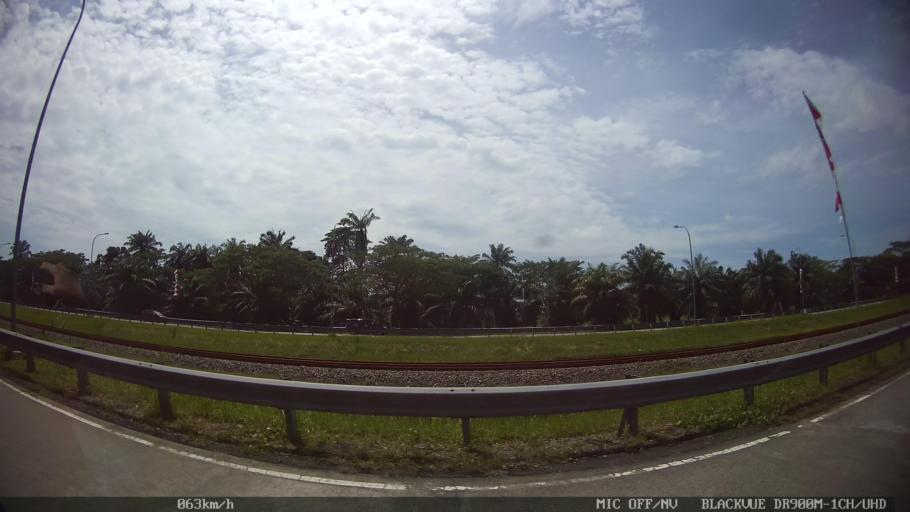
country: ID
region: North Sumatra
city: Percut
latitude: 3.6205
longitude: 98.8639
